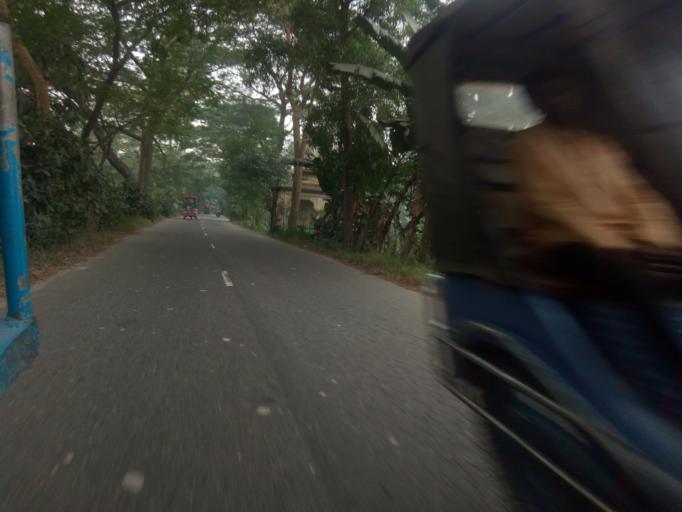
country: BD
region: Dhaka
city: Narayanganj
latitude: 23.5311
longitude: 90.4825
